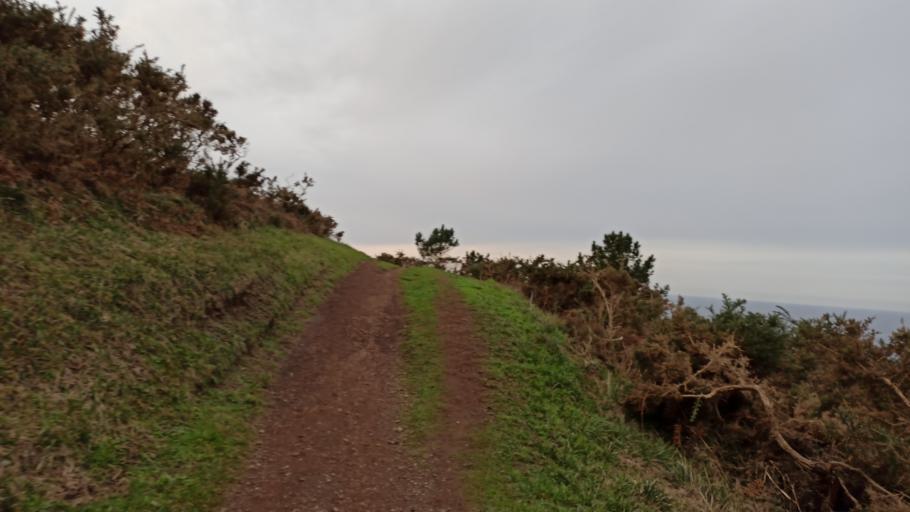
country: ES
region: Galicia
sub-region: Provincia da Coruna
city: A Coruna
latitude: 43.3970
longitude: -8.3364
